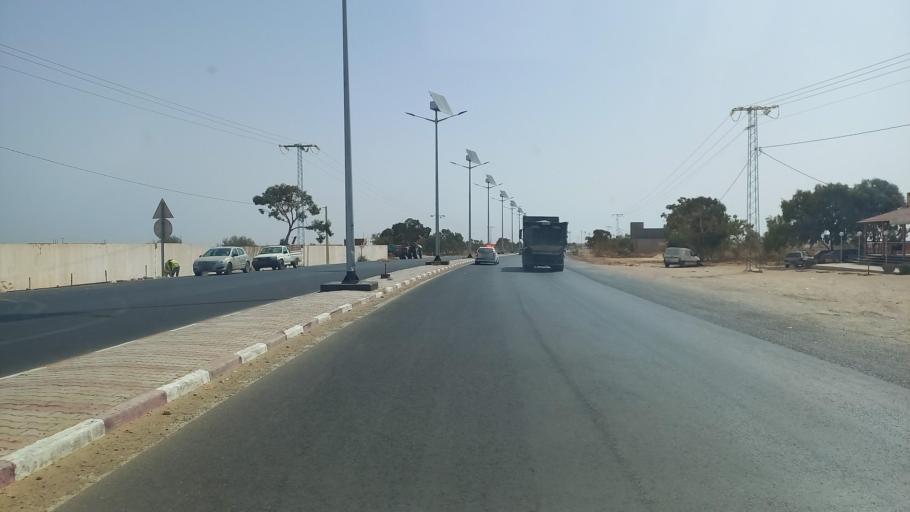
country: TN
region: Madanin
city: Medenine
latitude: 33.3605
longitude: 10.5566
